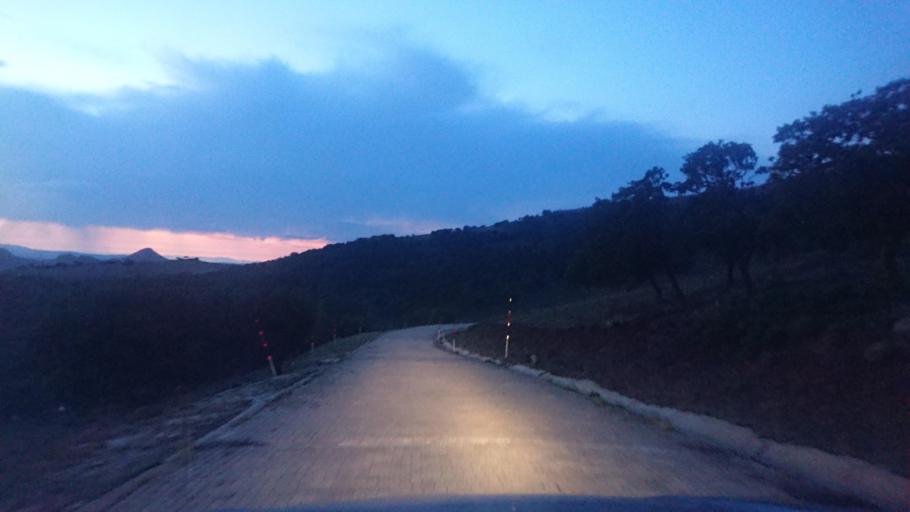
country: TR
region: Aksaray
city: Ortakoy
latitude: 38.6417
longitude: 34.0247
